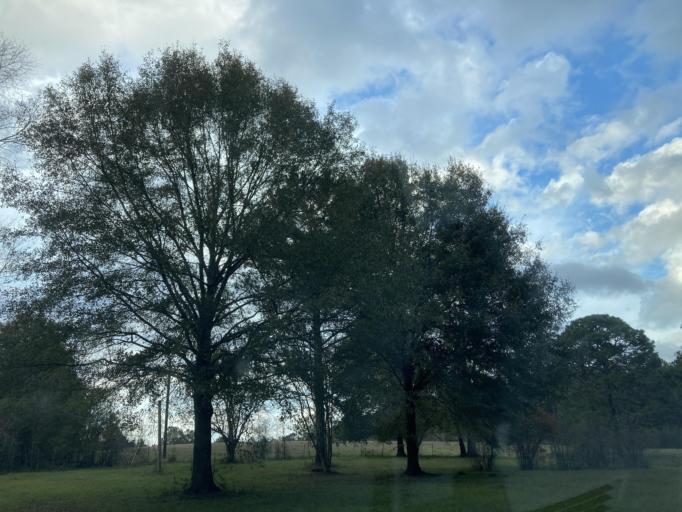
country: US
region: Mississippi
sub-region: Marion County
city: Columbia
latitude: 31.1933
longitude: -89.6448
